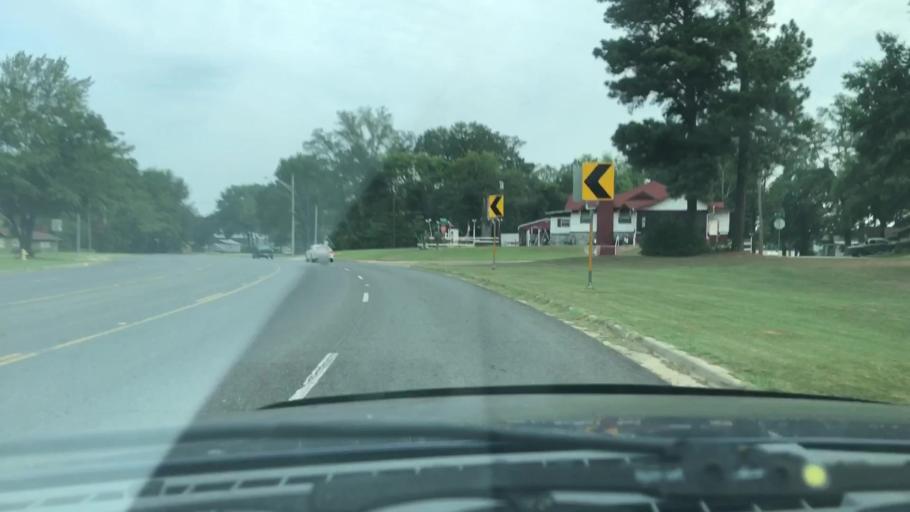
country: US
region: Texas
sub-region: Bowie County
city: Texarkana
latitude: 33.4323
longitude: -94.0618
